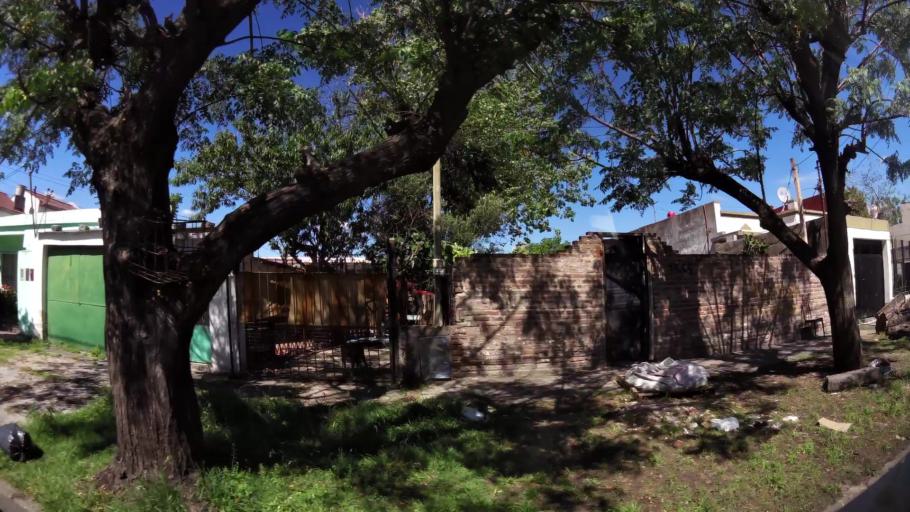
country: AR
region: Buenos Aires
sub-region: Partido de Lomas de Zamora
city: Lomas de Zamora
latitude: -34.7411
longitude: -58.4212
